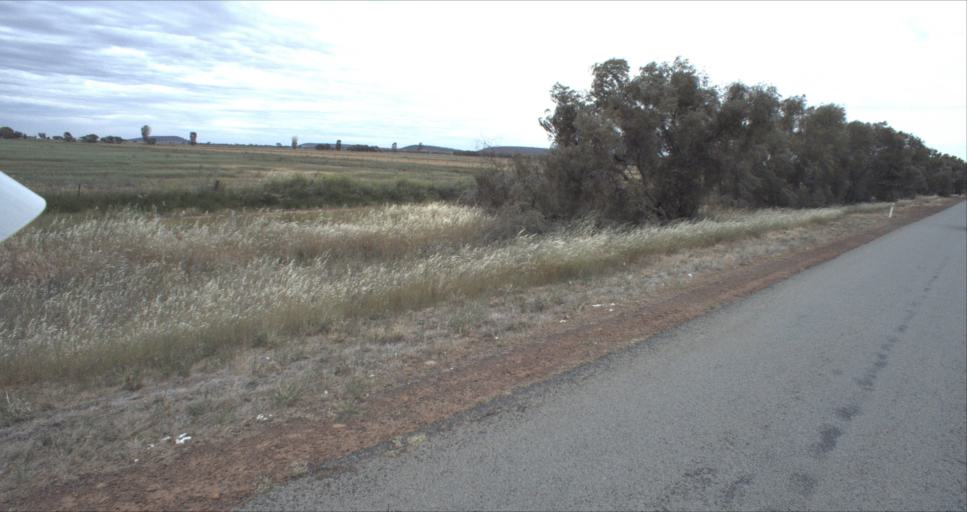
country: AU
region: New South Wales
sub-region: Leeton
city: Leeton
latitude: -34.4358
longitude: 146.3409
